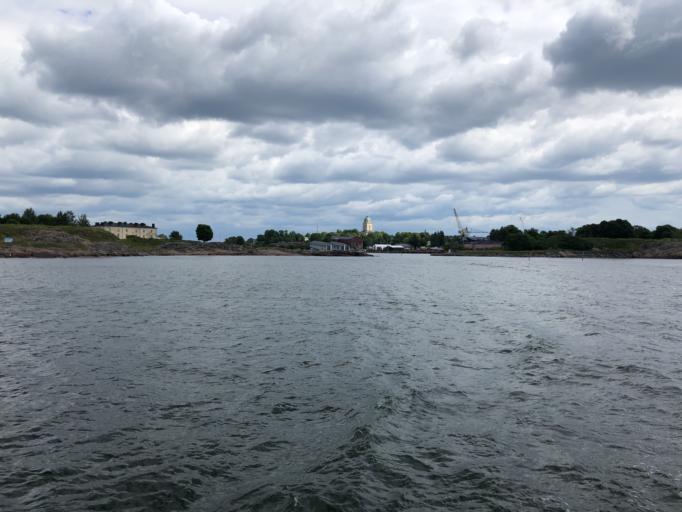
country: FI
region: Uusimaa
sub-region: Helsinki
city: Helsinki
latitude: 60.1445
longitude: 24.9722
